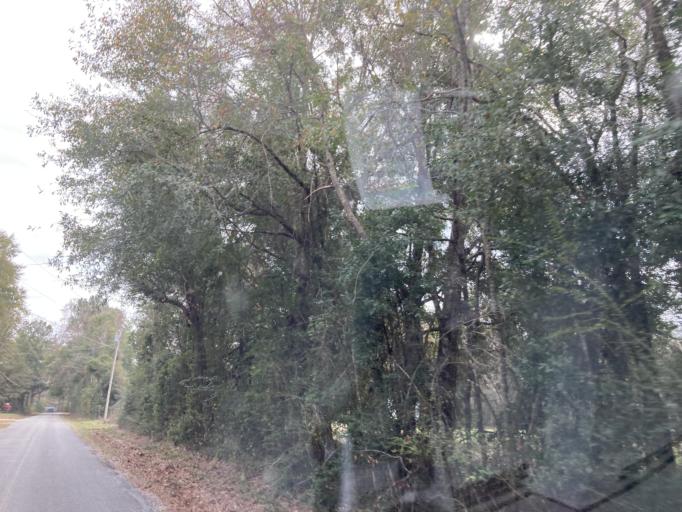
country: US
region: Mississippi
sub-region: Stone County
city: Wiggins
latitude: 31.0640
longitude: -89.2060
